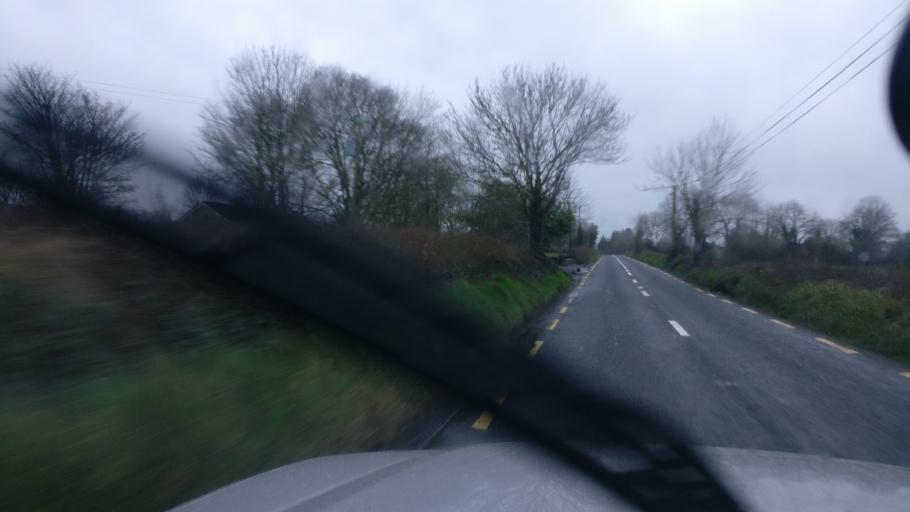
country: IE
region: Connaught
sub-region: County Galway
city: Portumna
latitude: 53.1301
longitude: -8.2077
